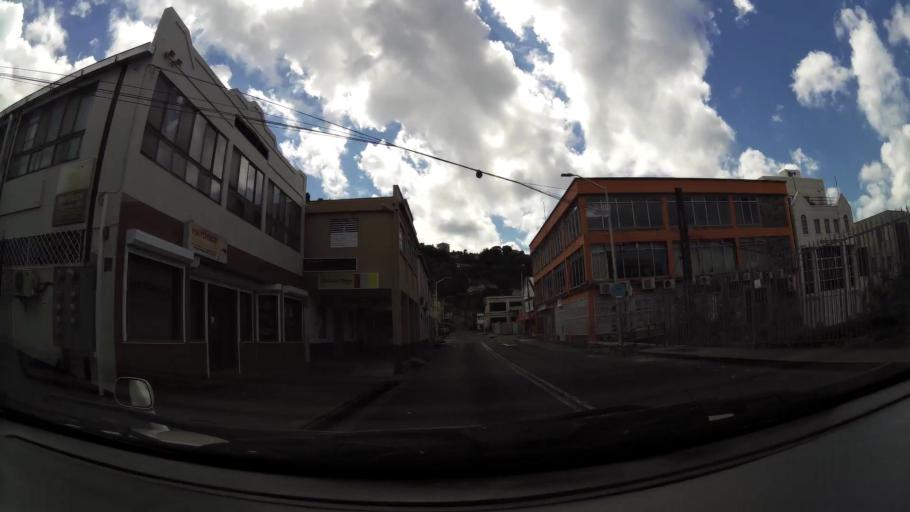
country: VC
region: Saint George
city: Kingstown
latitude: 13.1530
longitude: -61.2229
